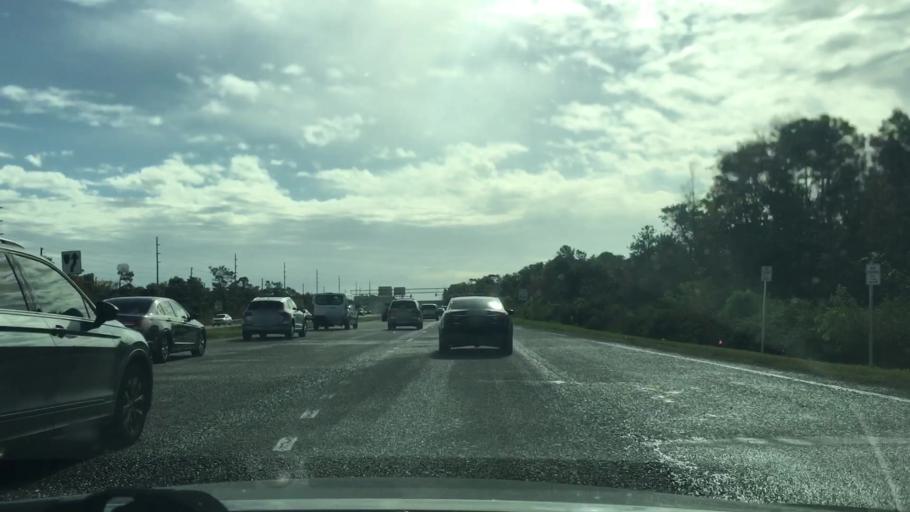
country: US
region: Florida
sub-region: Osceola County
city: Celebration
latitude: 28.3572
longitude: -81.4971
